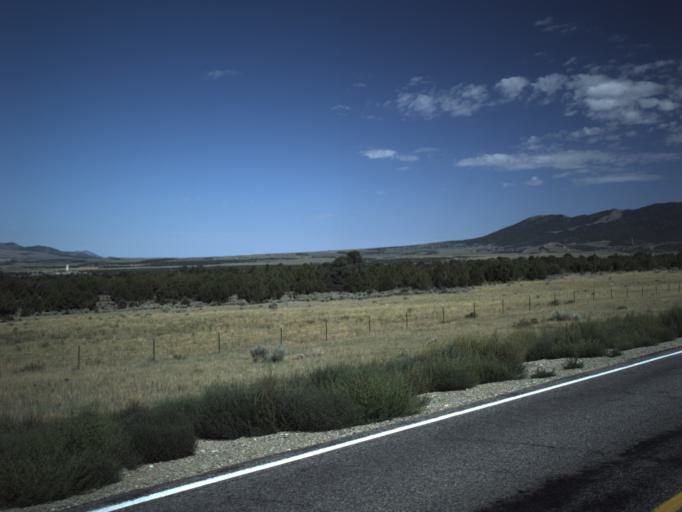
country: US
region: Utah
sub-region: Utah County
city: Genola
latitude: 39.9298
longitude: -112.1483
